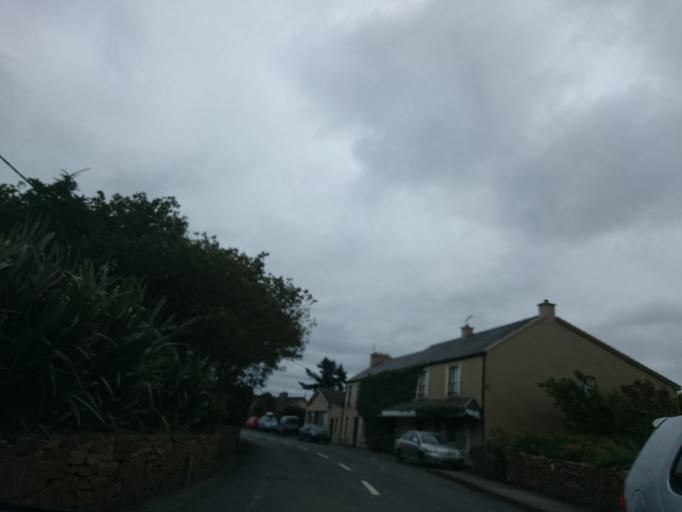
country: IE
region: Connaught
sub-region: County Galway
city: Clifden
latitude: 53.5561
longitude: -10.1109
